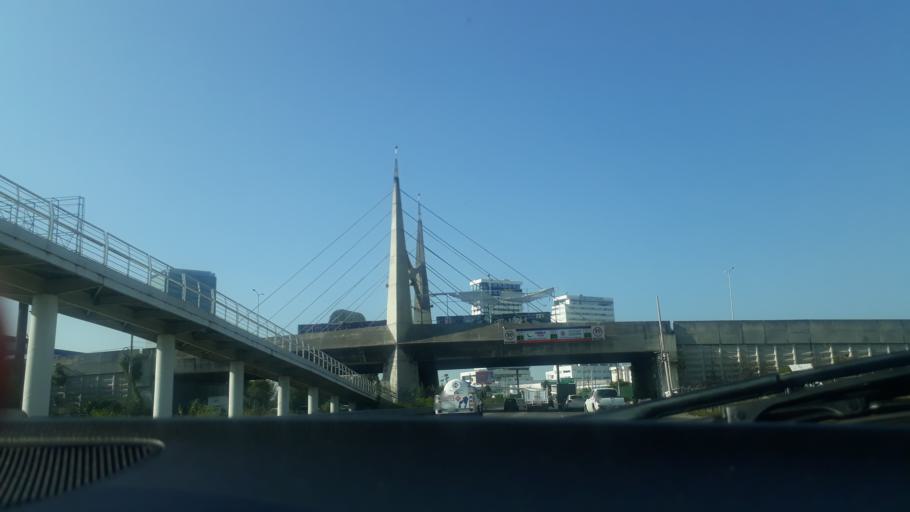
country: MX
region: Puebla
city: Tlazcalancingo
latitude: 19.0156
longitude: -98.2642
